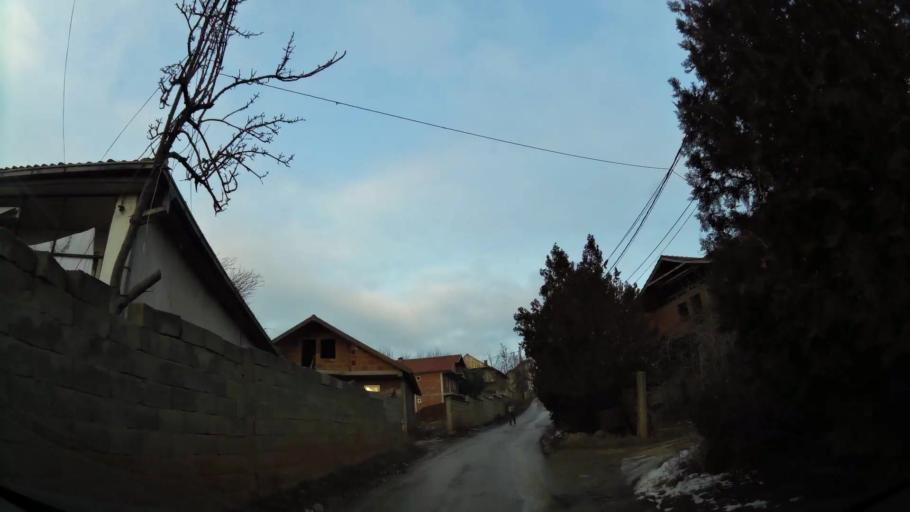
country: MK
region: Aracinovo
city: Arachinovo
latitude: 42.0288
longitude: 21.5754
